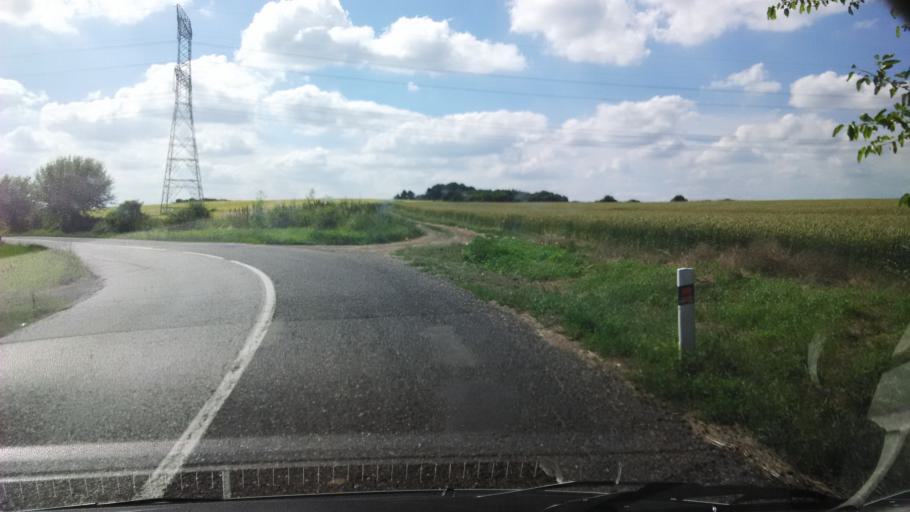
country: SK
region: Nitriansky
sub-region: Okres Nitra
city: Vrable
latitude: 48.1540
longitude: 18.4313
